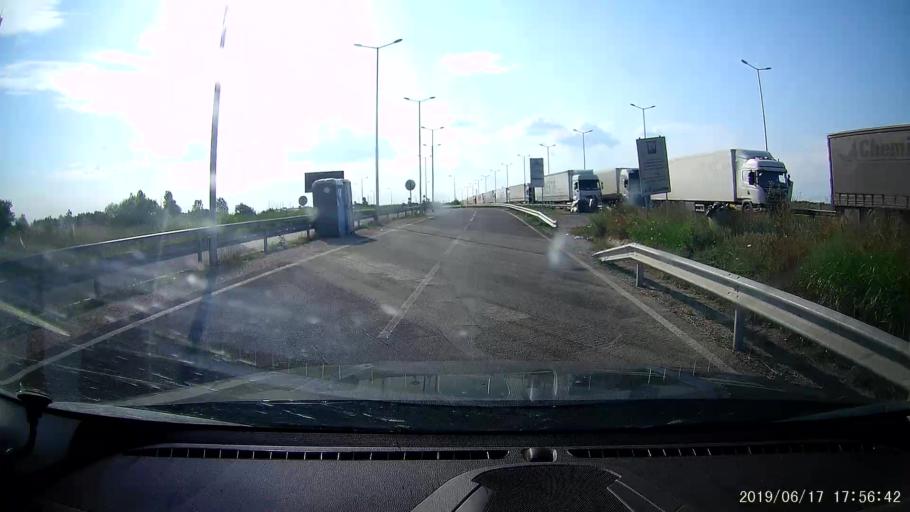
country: GR
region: East Macedonia and Thrace
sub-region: Nomos Evrou
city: Rizia
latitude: 41.7195
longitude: 26.3443
